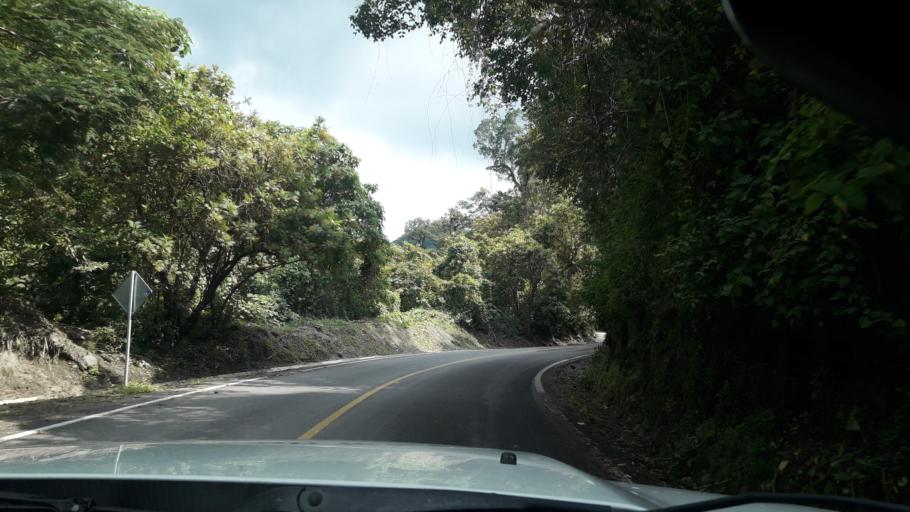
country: MX
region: Colima
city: Suchitlan
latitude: 19.4392
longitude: -103.7128
